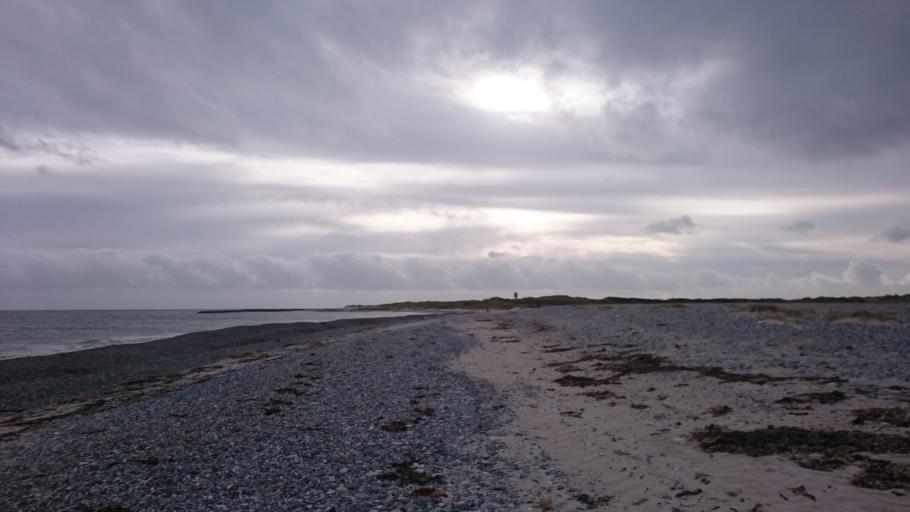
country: DE
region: Schleswig-Holstein
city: Helgoland
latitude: 54.1880
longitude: 7.9194
